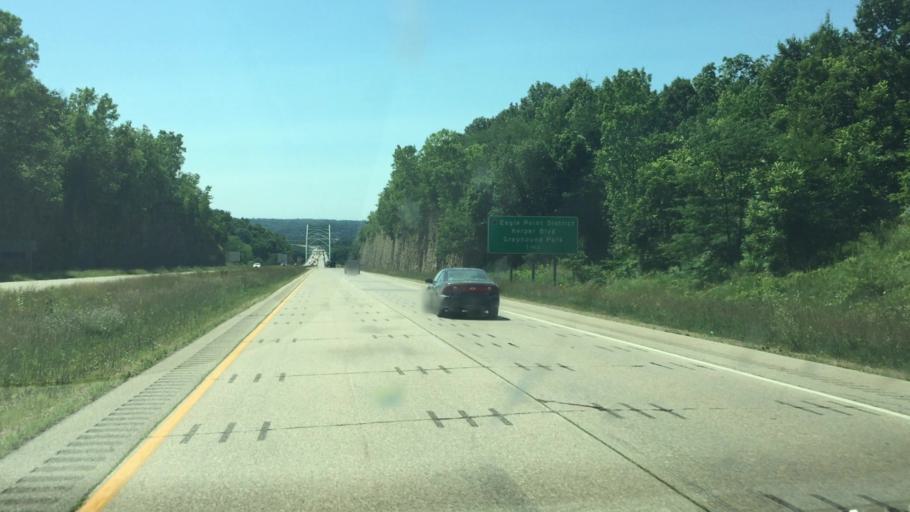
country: US
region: Illinois
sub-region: Jo Daviess County
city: East Dubuque
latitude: 42.5153
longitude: -90.6226
